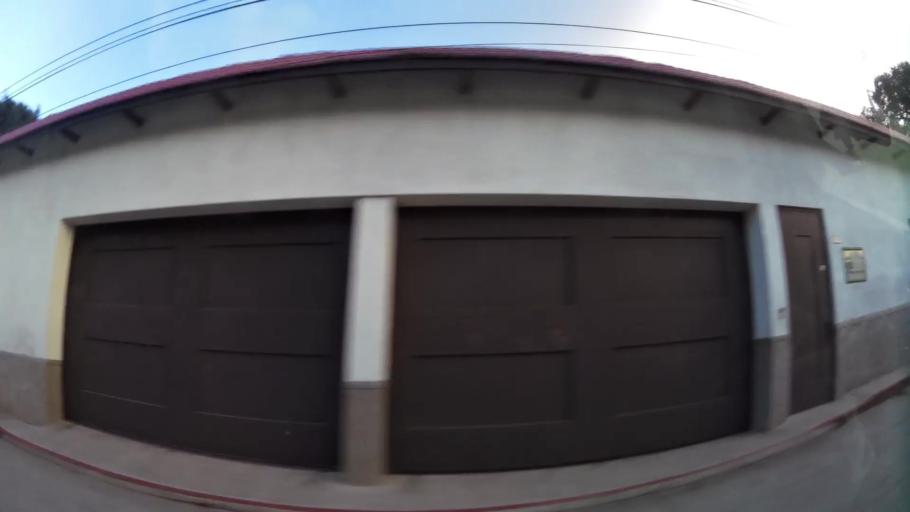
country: GT
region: Sacatepequez
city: San Bartolome Milpas Altas
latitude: 14.6089
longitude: -90.6688
